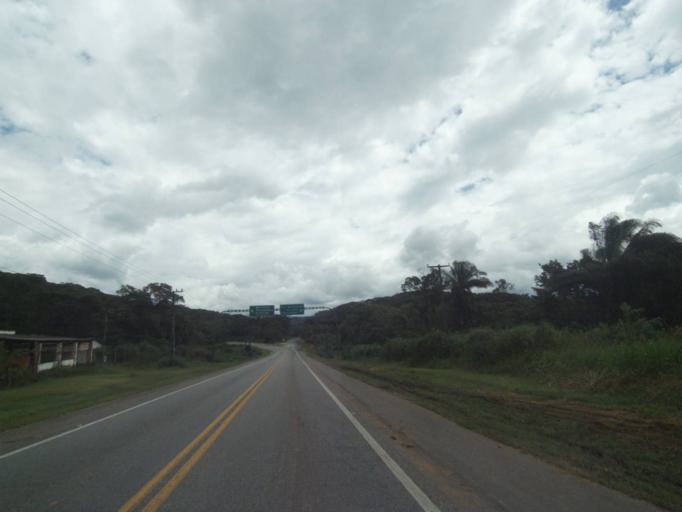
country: BR
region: Parana
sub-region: Antonina
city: Antonina
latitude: -25.4446
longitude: -48.7835
